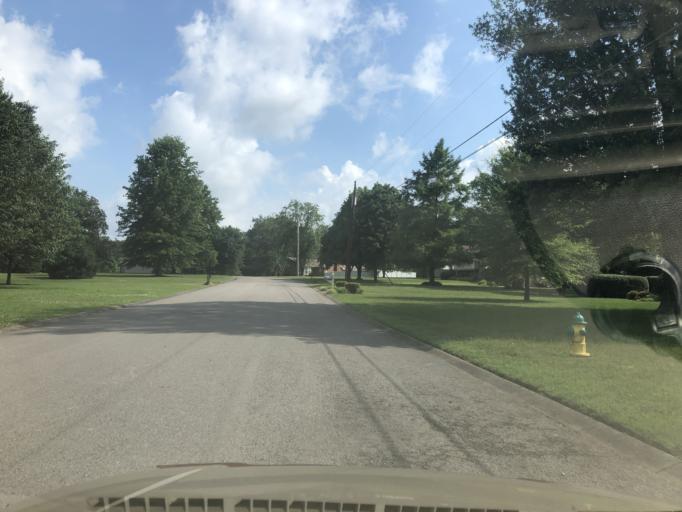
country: US
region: Tennessee
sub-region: Wilson County
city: Green Hill
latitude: 36.2341
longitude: -86.5830
